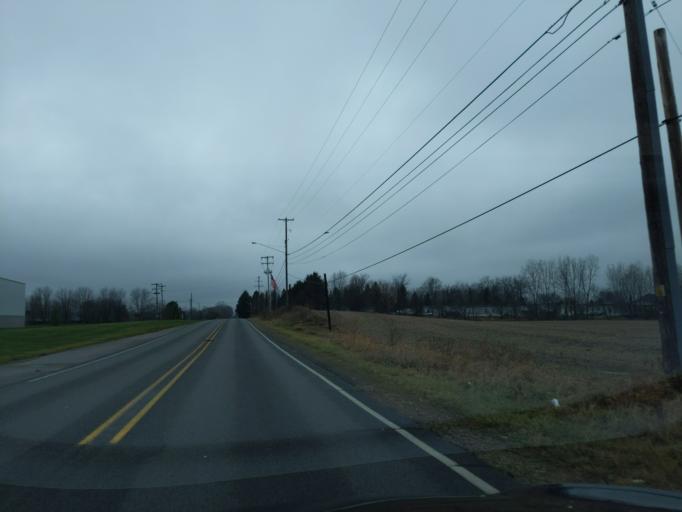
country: US
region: Michigan
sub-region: Jackson County
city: Jackson
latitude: 42.2766
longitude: -84.4703
